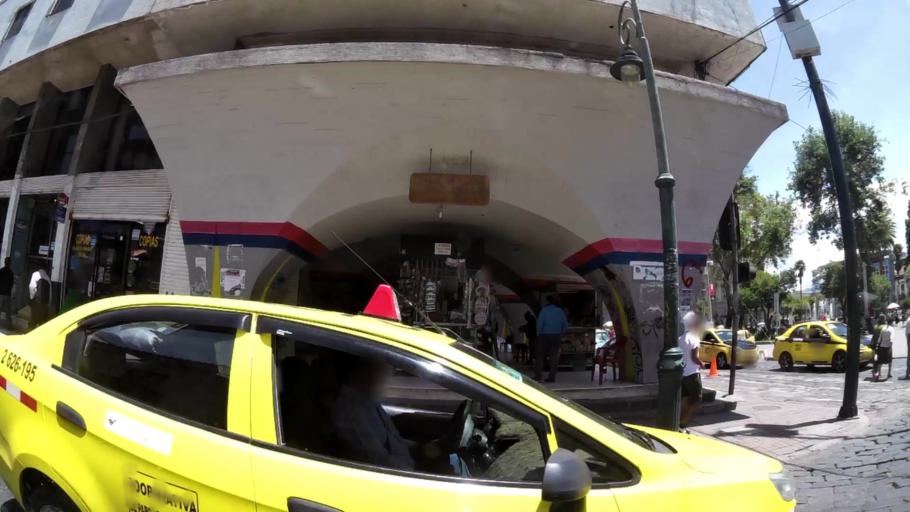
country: EC
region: Chimborazo
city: Riobamba
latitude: -1.6718
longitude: -78.6510
